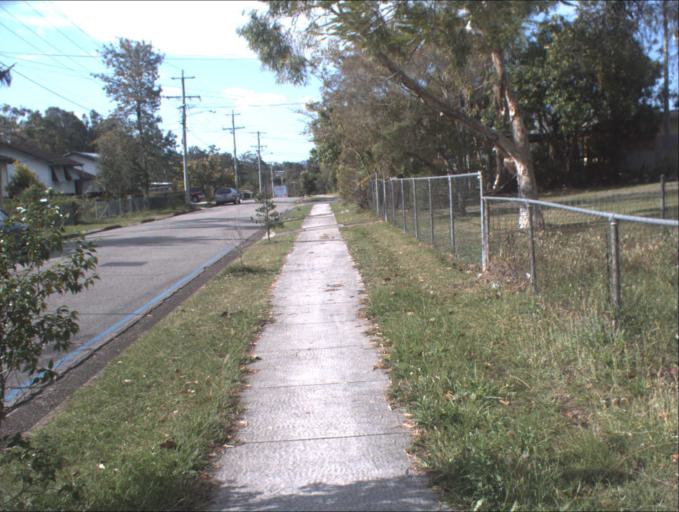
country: AU
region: Queensland
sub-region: Logan
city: Woodridge
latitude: -27.6271
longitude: 153.0972
